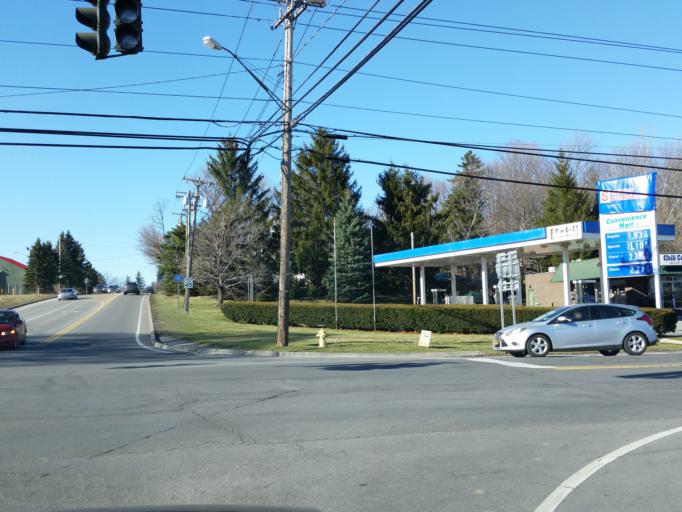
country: US
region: New York
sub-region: Monroe County
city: Scottsville
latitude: 43.0930
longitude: -77.7979
